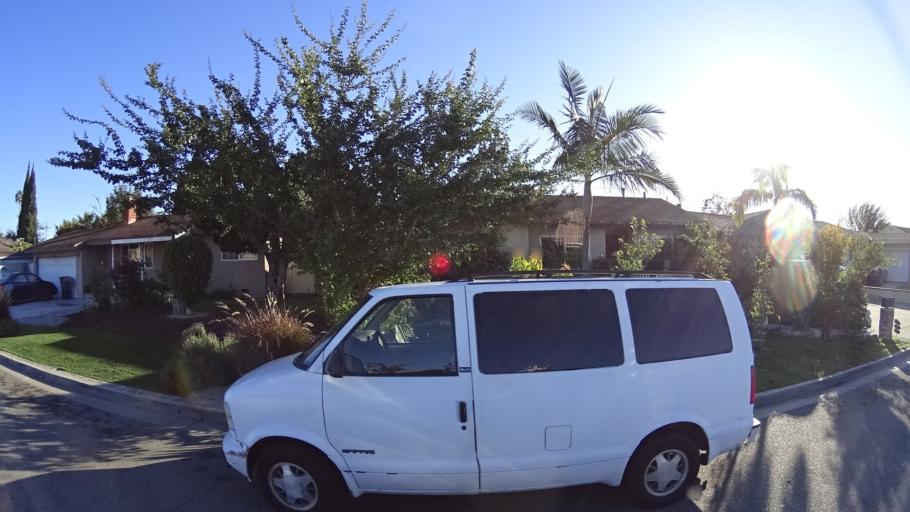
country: US
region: California
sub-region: Orange County
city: Midway City
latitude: 33.7693
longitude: -117.9751
